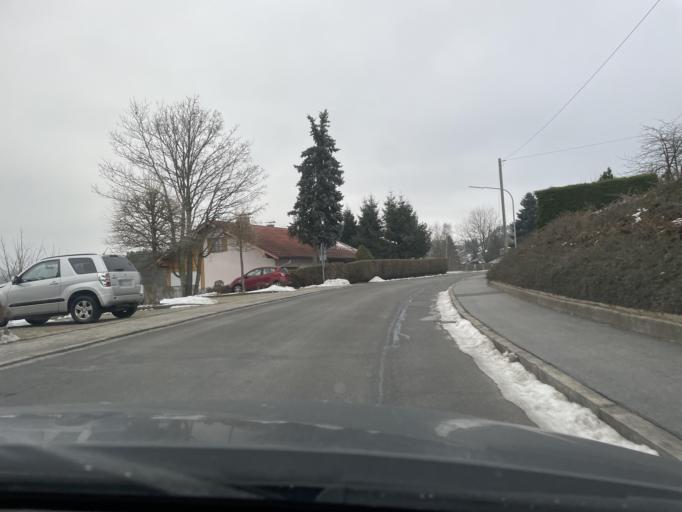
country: DE
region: Bavaria
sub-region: Lower Bavaria
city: Viechtach
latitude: 49.0701
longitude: 12.8976
